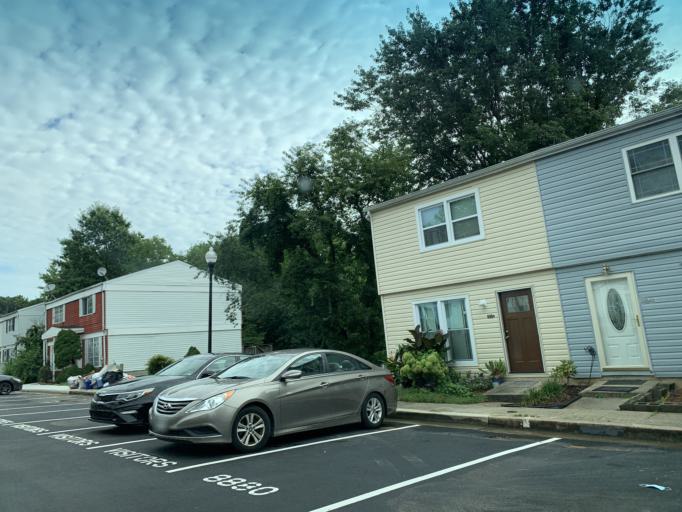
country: US
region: Maryland
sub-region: Baltimore County
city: Rossville
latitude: 39.3461
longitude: -76.4841
